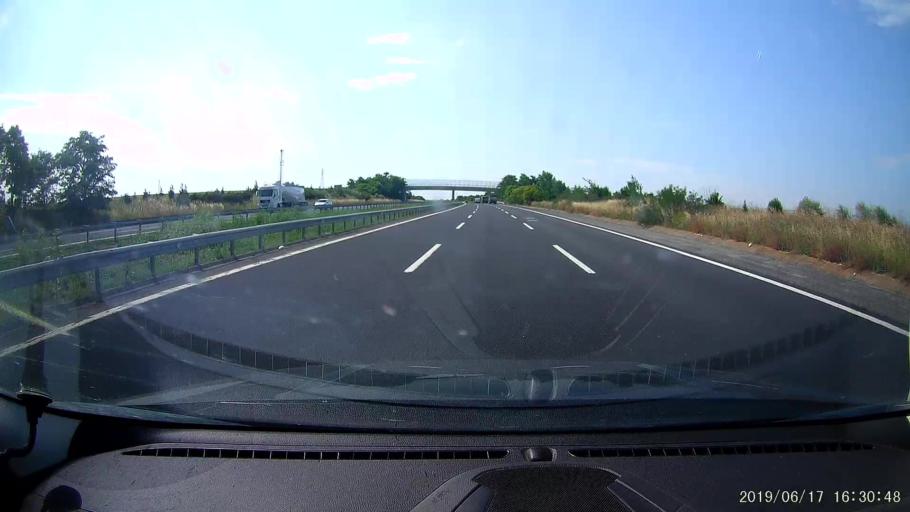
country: TR
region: Tekirdag
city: Beyazkoy
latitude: 41.3533
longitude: 27.6457
